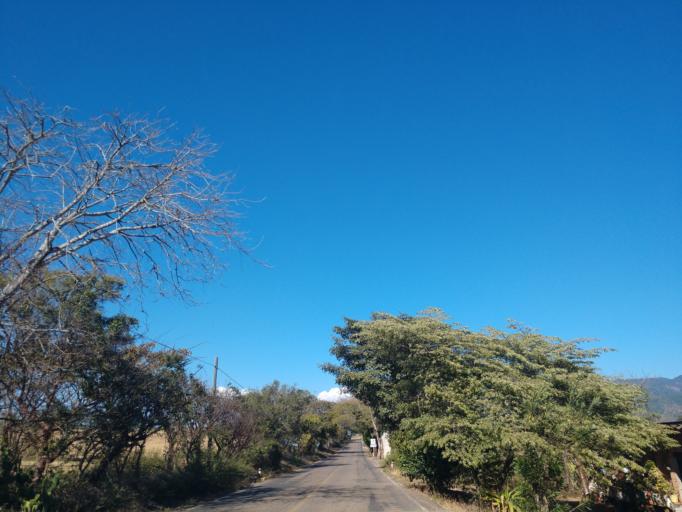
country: MX
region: Nayarit
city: Compostela
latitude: 21.2559
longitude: -104.8997
